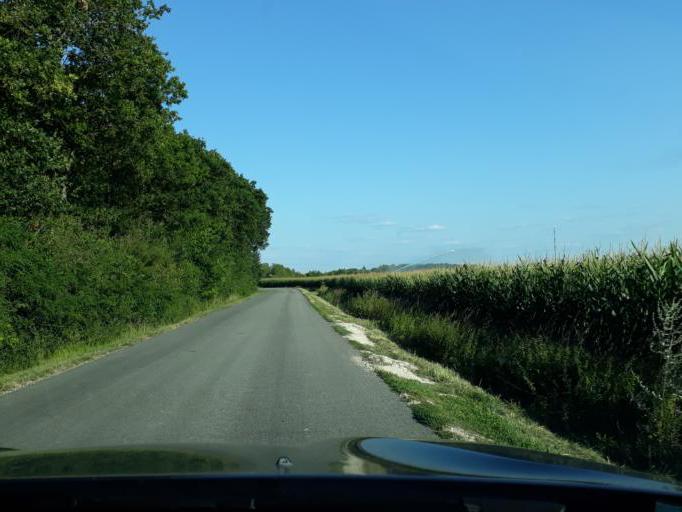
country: FR
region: Centre
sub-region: Departement du Loiret
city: Huisseau-sur-Mauves
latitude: 47.8808
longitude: 1.7286
